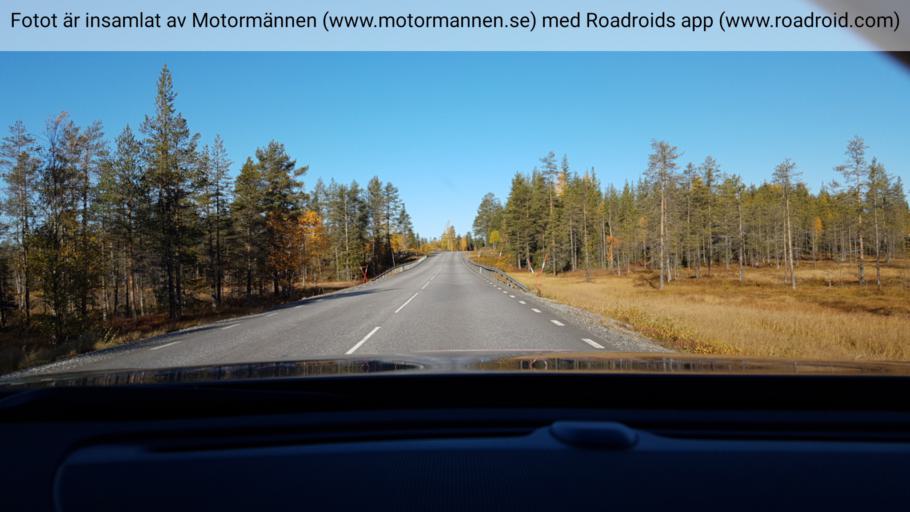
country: SE
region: Vaesterbotten
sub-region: Skelleftea Kommun
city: Storvik
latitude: 65.3321
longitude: 20.5882
